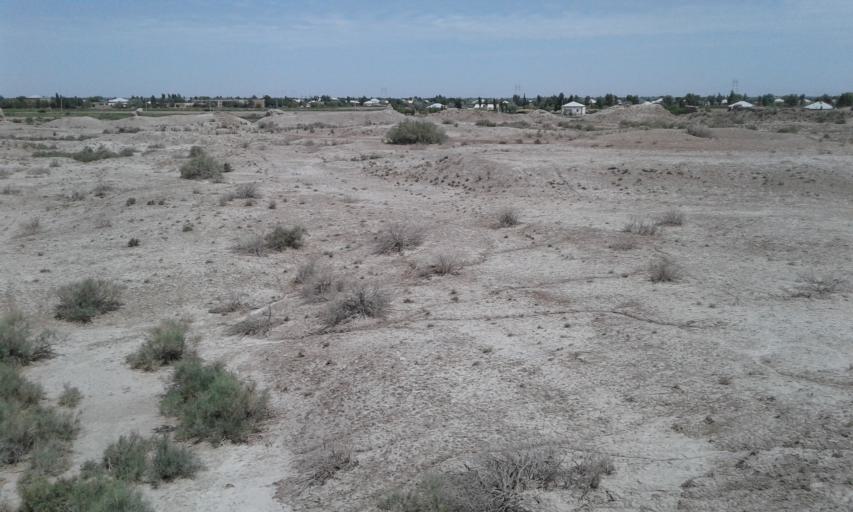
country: TM
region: Dasoguz
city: Tagta
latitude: 41.5406
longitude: 59.9994
